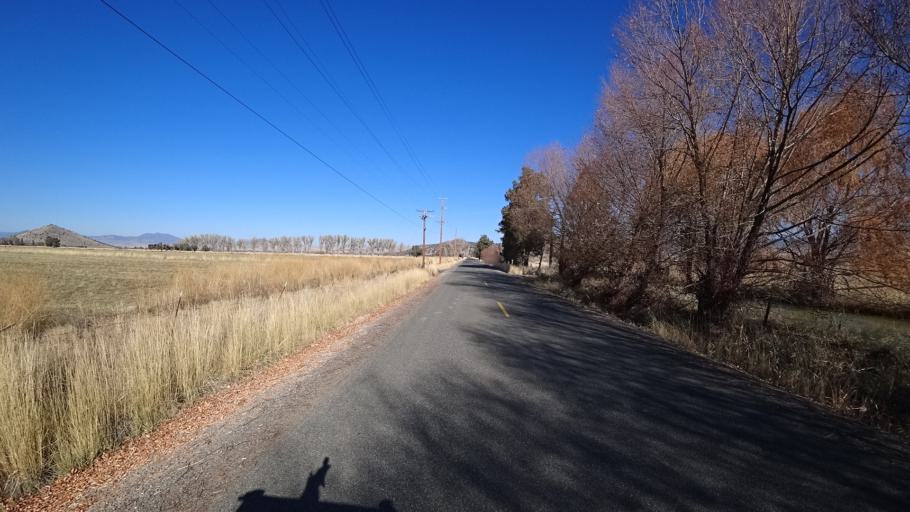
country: US
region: California
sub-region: Siskiyou County
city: Montague
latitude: 41.6790
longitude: -122.3698
